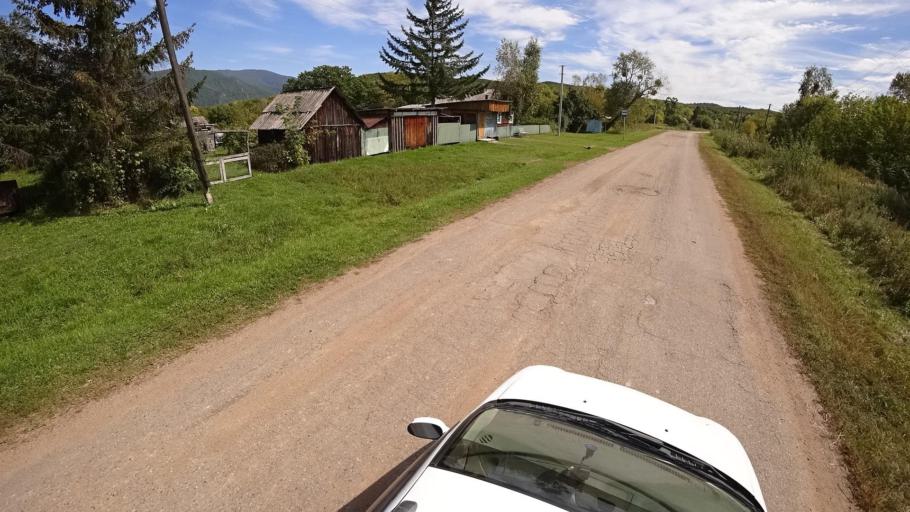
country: RU
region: Primorskiy
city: Yakovlevka
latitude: 44.6560
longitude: 133.7425
